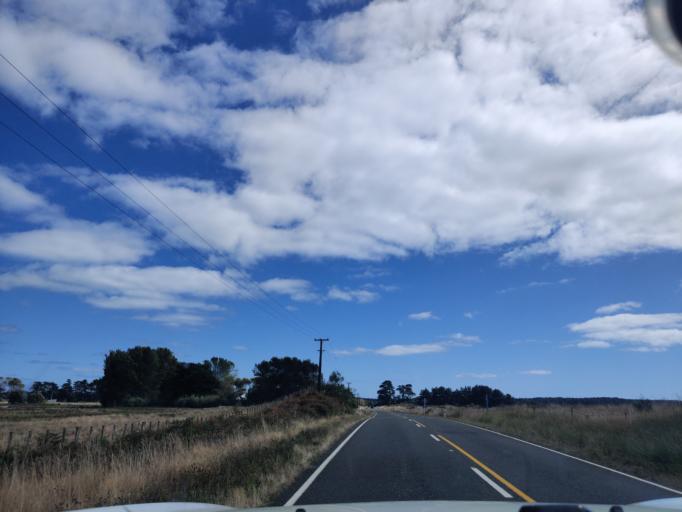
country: NZ
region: Manawatu-Wanganui
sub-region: Horowhenua District
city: Foxton
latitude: -40.3853
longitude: 175.2779
